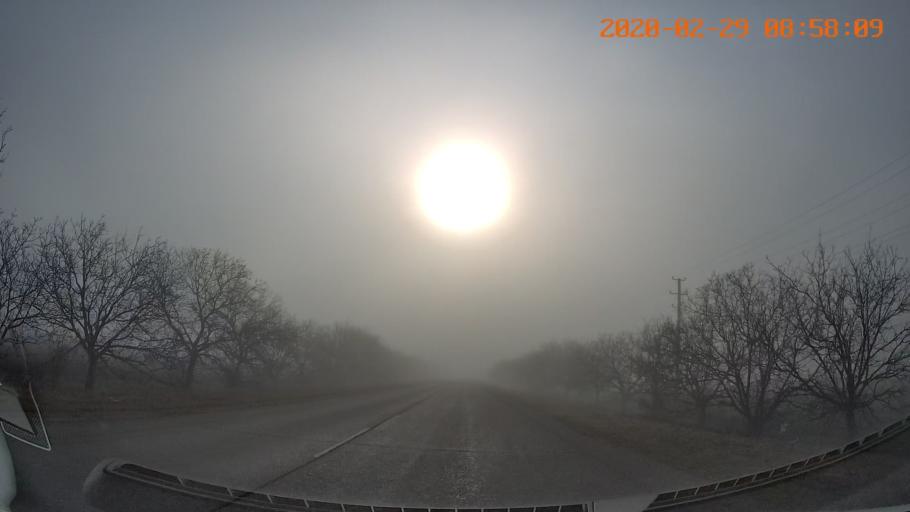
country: MD
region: Telenesti
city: Tiraspolul Nou
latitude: 46.9229
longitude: 29.6367
